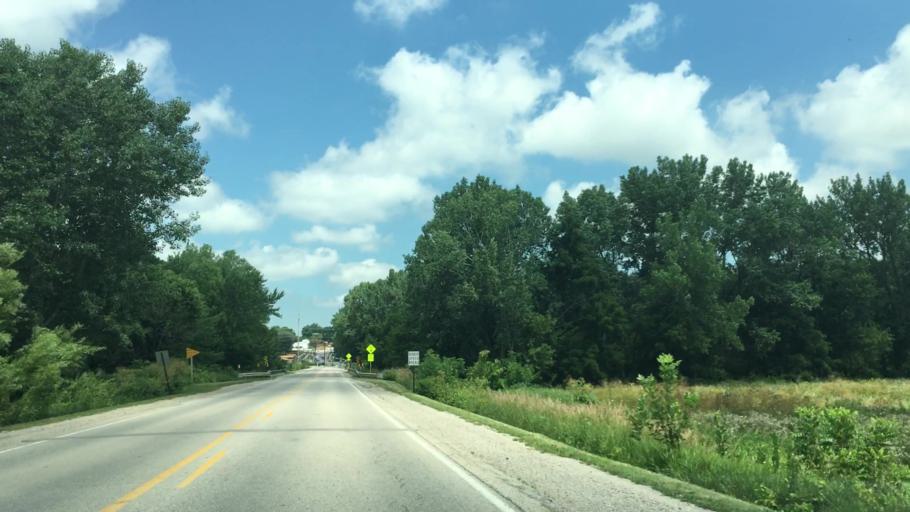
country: US
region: Iowa
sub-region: Johnson County
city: Tiffin
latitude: 41.6997
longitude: -91.6665
